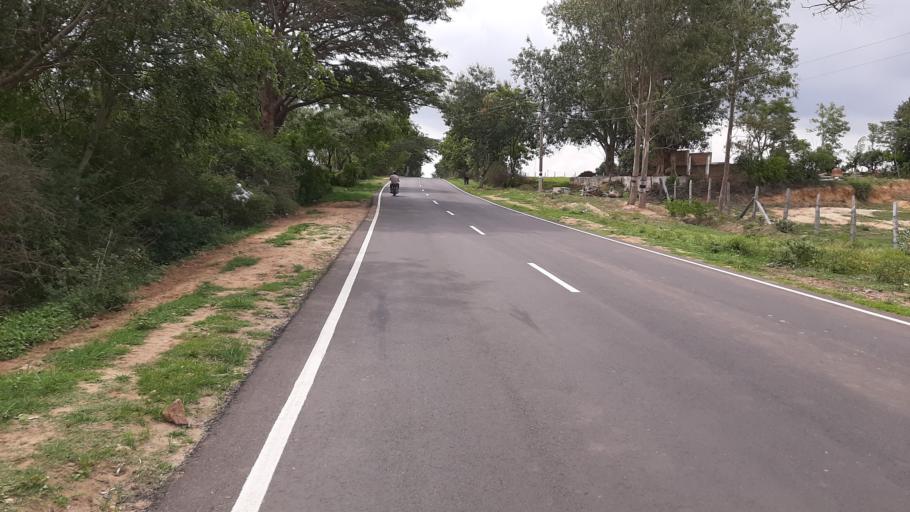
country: IN
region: Tamil Nadu
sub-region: Krishnagiri
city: Denkanikota
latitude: 12.5335
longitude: 77.7776
